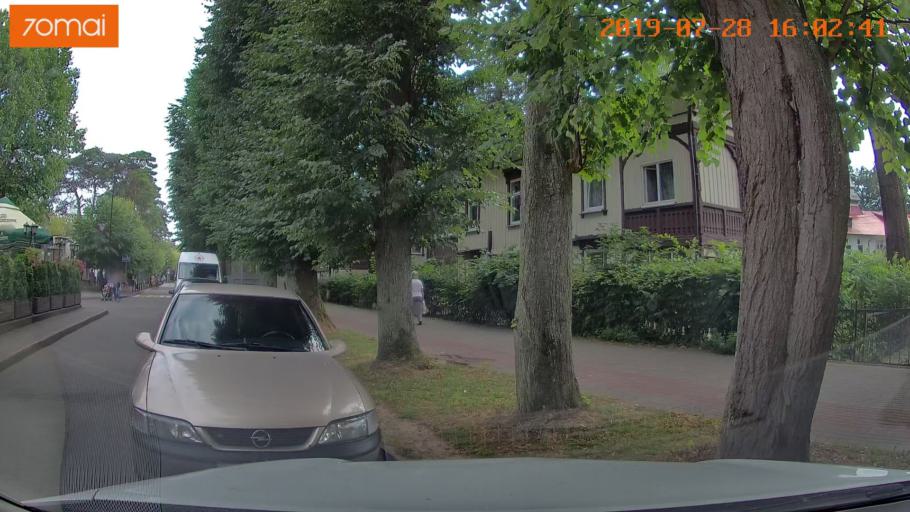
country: RU
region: Kaliningrad
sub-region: Gorod Svetlogorsk
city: Svetlogorsk
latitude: 54.9448
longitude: 20.1523
